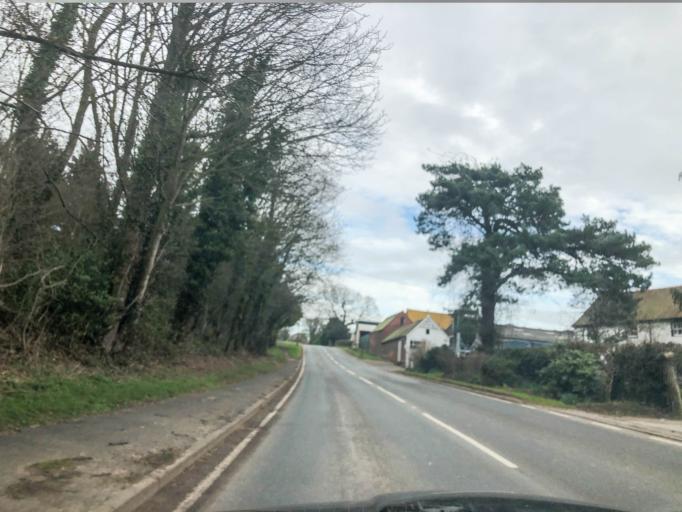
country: GB
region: England
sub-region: Warwickshire
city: Wroxall
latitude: 52.3019
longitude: -1.6653
